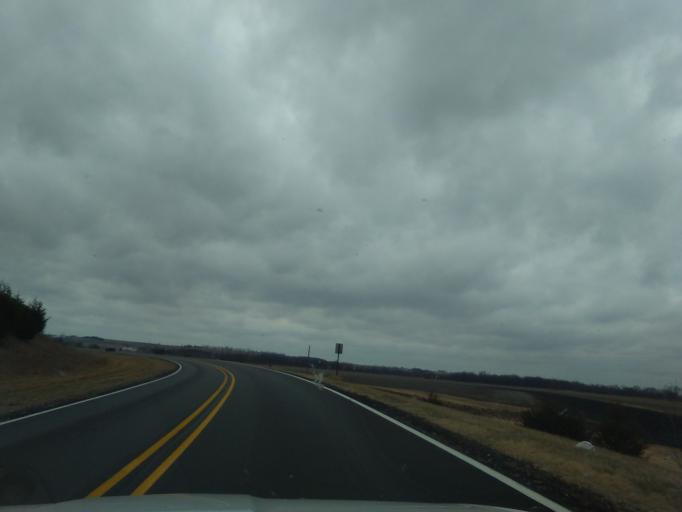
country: US
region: Kansas
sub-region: Nemaha County
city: Sabetha
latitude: 40.0649
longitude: -95.7846
